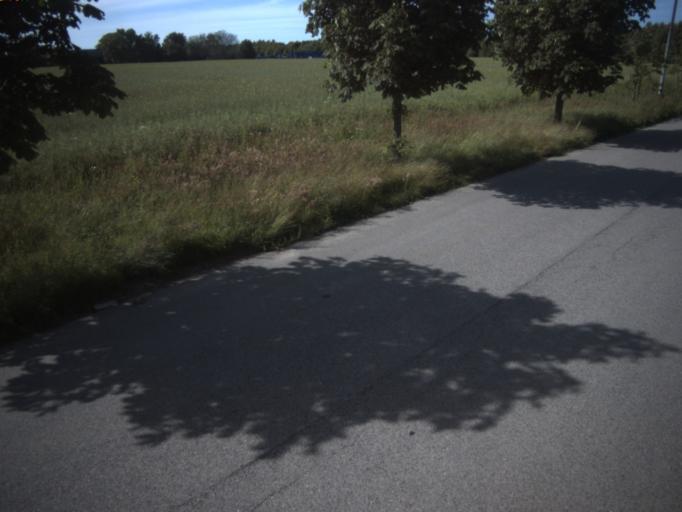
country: SE
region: Skane
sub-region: Helsingborg
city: Odakra
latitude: 56.0787
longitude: 12.7545
